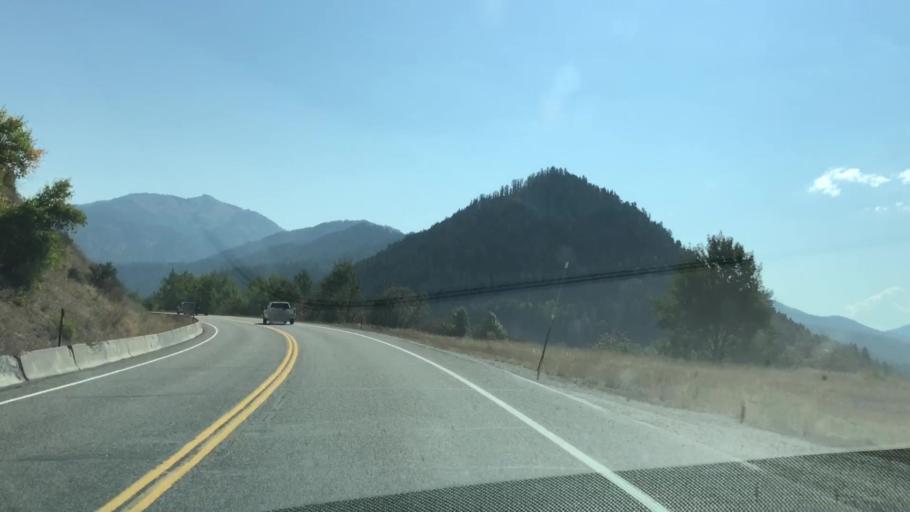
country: US
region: Idaho
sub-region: Teton County
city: Victor
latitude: 43.3189
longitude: -111.1540
